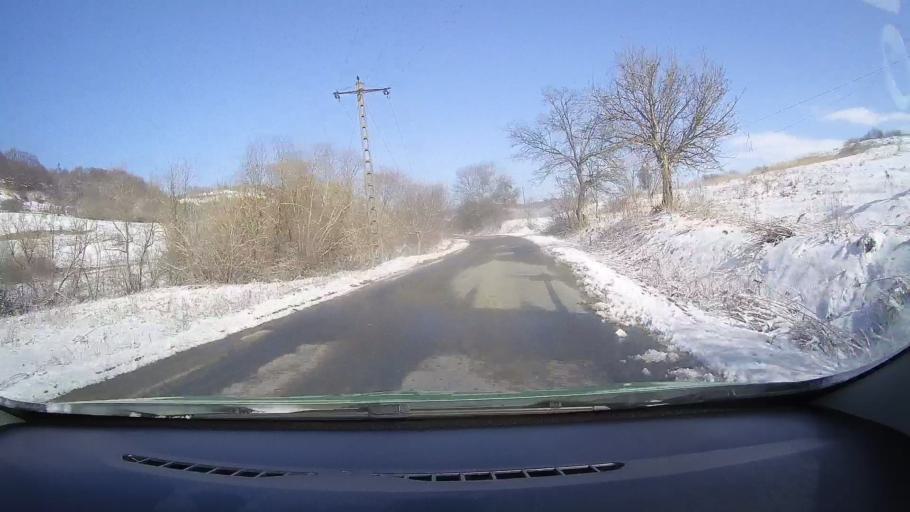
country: RO
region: Sibiu
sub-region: Comuna Mihaileni
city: Mihaileni
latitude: 46.0136
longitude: 24.3757
